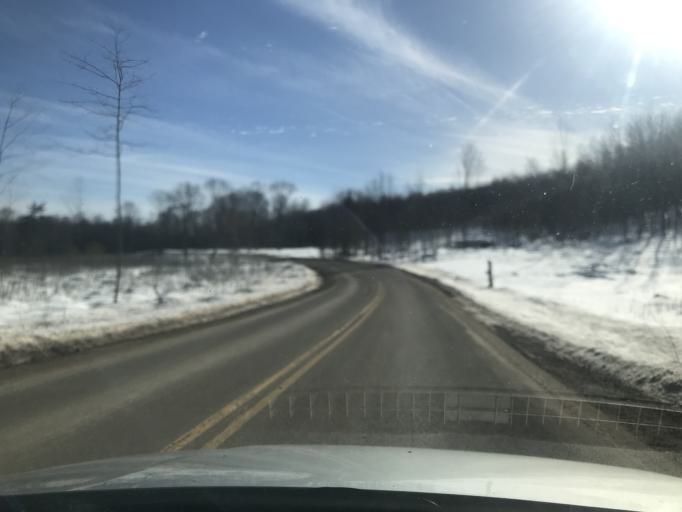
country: US
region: Michigan
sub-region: Dickinson County
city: Kingsford
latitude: 45.4046
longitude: -88.3792
